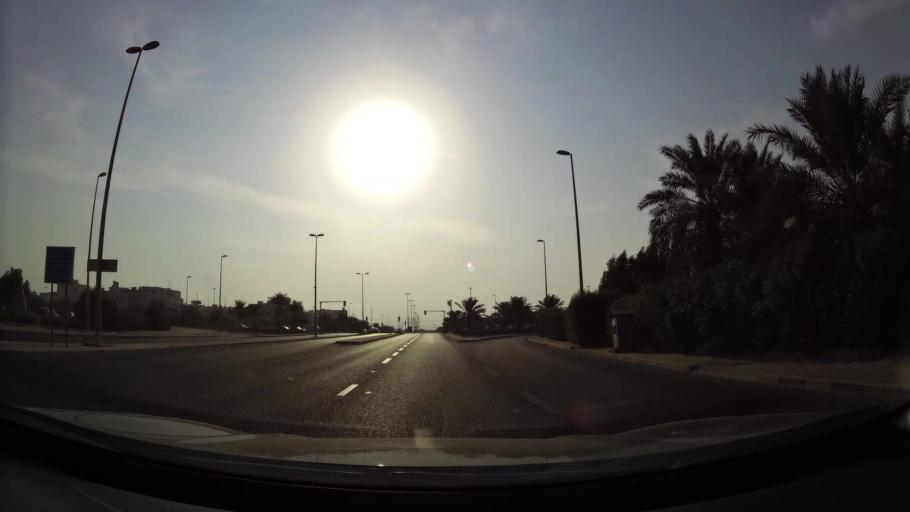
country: KW
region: Mubarak al Kabir
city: Mubarak al Kabir
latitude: 29.1946
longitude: 48.0701
